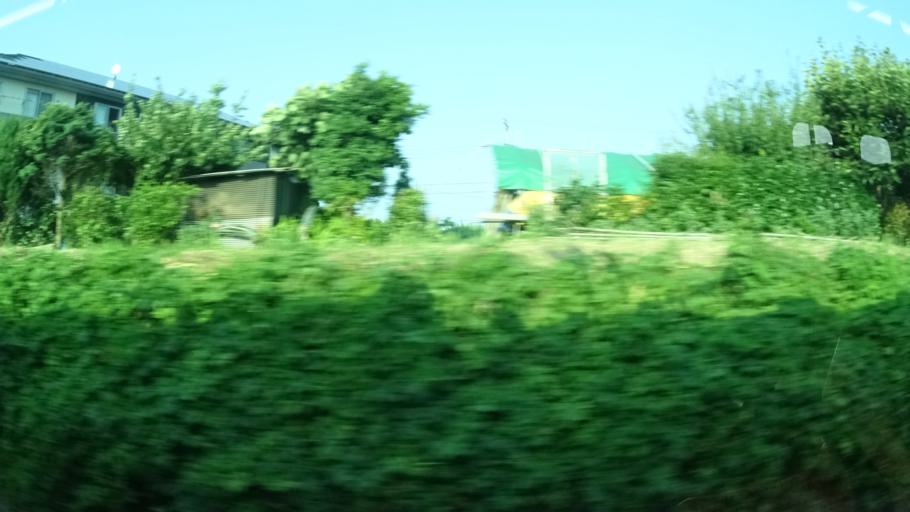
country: JP
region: Ibaraki
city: Hitachi
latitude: 36.6414
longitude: 140.6739
